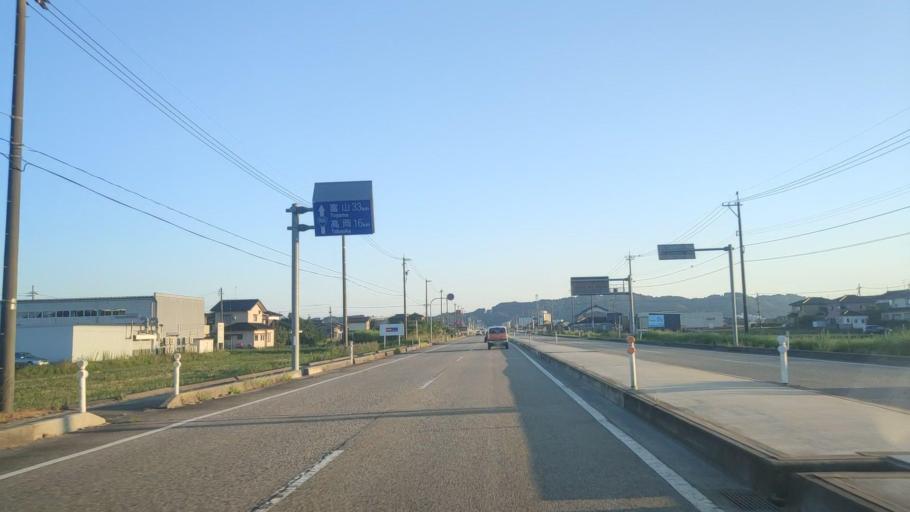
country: JP
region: Toyama
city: Himi
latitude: 36.8736
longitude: 136.9752
